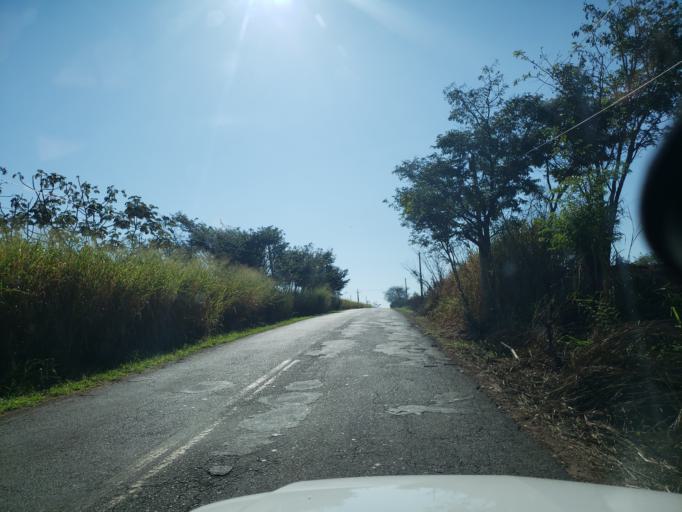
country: BR
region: Sao Paulo
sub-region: Moji-Guacu
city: Mogi-Gaucu
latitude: -22.3506
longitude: -46.8962
